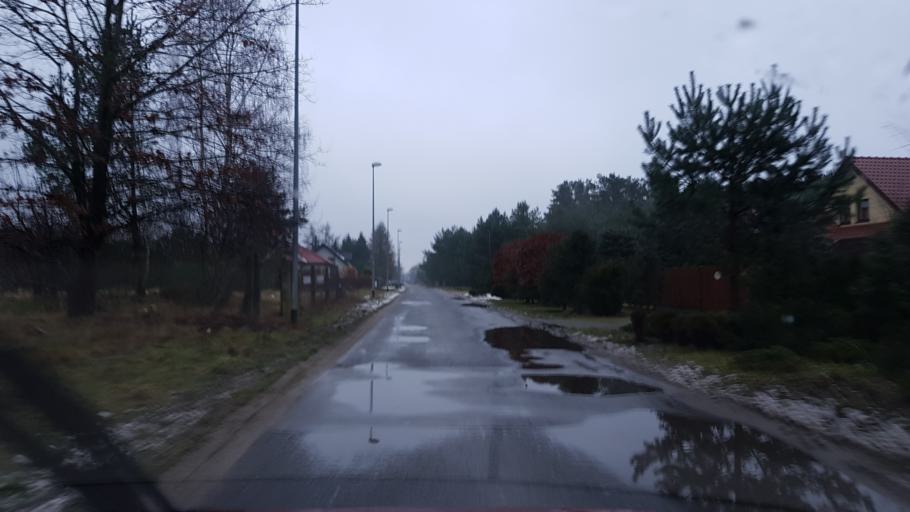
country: PL
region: West Pomeranian Voivodeship
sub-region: Powiat policki
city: Dobra
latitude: 53.5483
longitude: 14.4524
